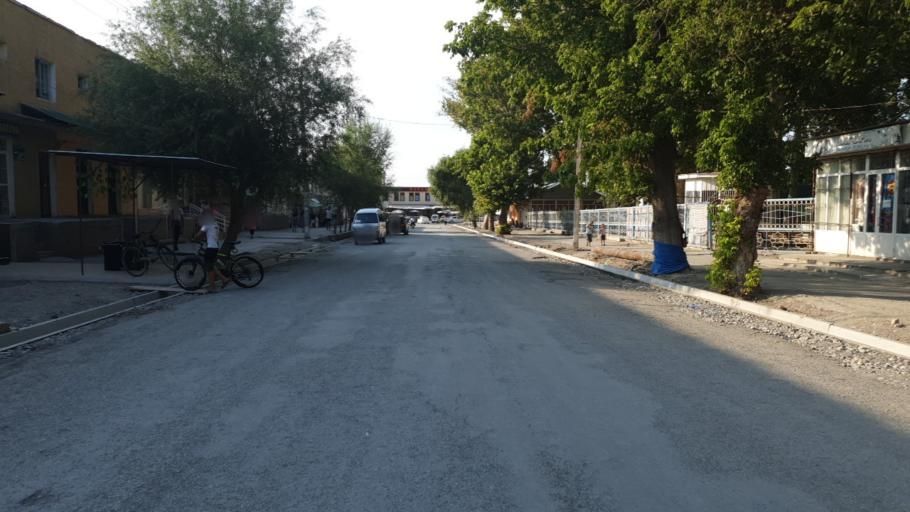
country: UZ
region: Fergana
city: Yaypan
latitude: 40.3795
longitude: 70.8106
